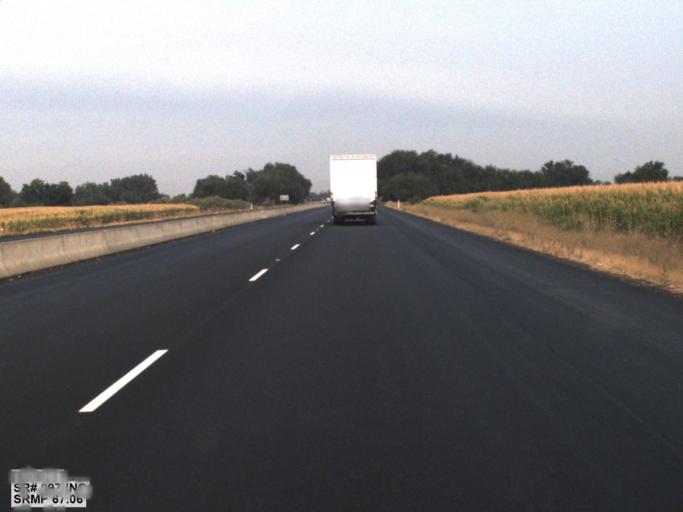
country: US
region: Washington
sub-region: Yakima County
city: Wapato
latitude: 46.4247
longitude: -120.4066
